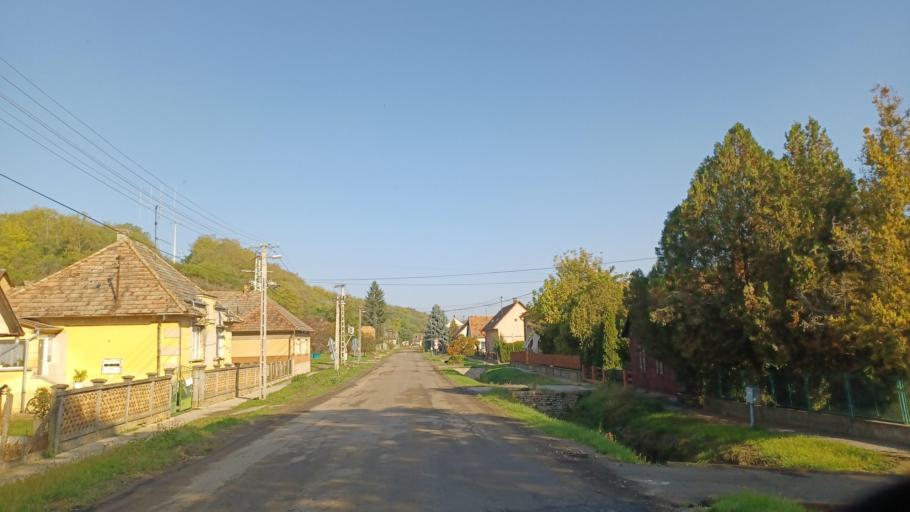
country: HU
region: Tolna
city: Szedres
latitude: 46.5110
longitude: 18.5904
